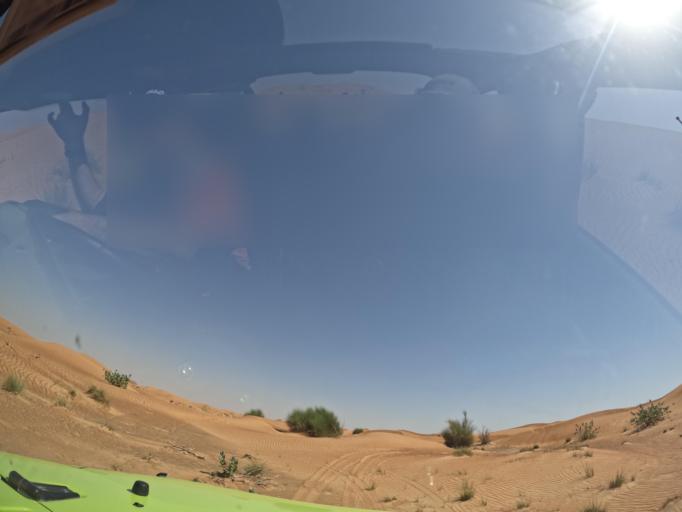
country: AE
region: Ash Shariqah
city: Adh Dhayd
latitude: 24.9790
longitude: 55.7260
